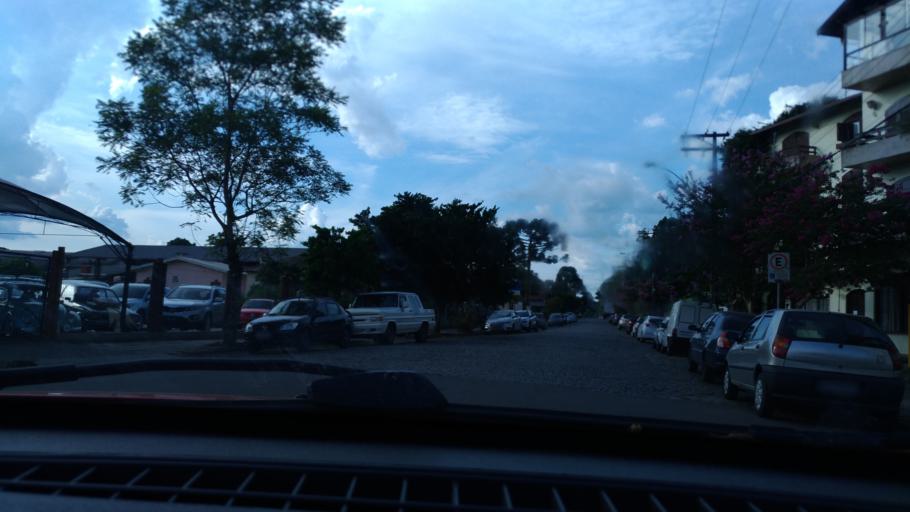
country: BR
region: Rio Grande do Sul
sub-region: Canela
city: Canela
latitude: -29.3589
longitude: -50.8127
